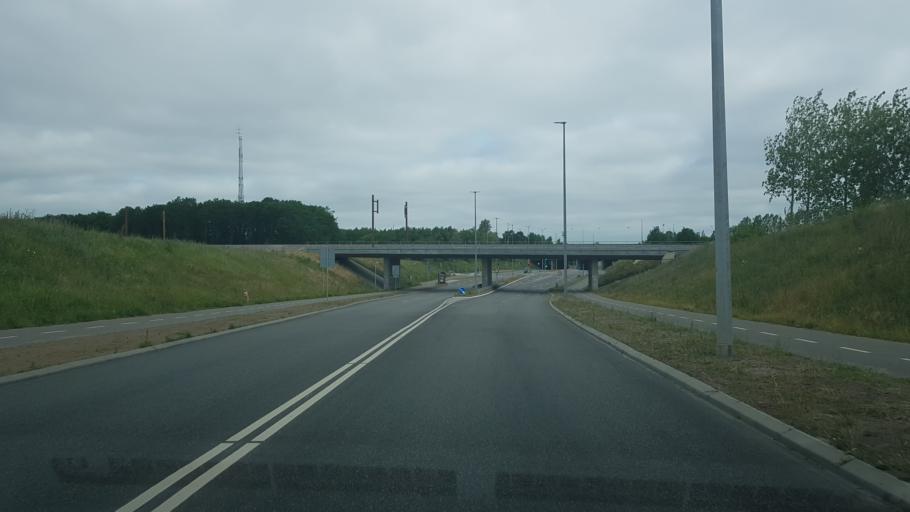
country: DK
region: Capital Region
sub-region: Brondby Kommune
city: Brondbyvester
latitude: 55.6383
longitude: 12.4185
